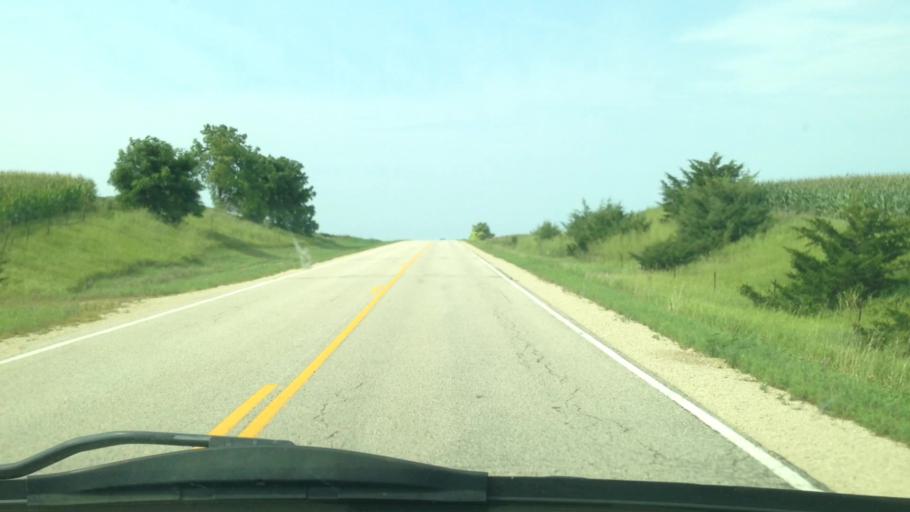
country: US
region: Minnesota
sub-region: Winona County
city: Saint Charles
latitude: 43.8671
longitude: -91.9594
